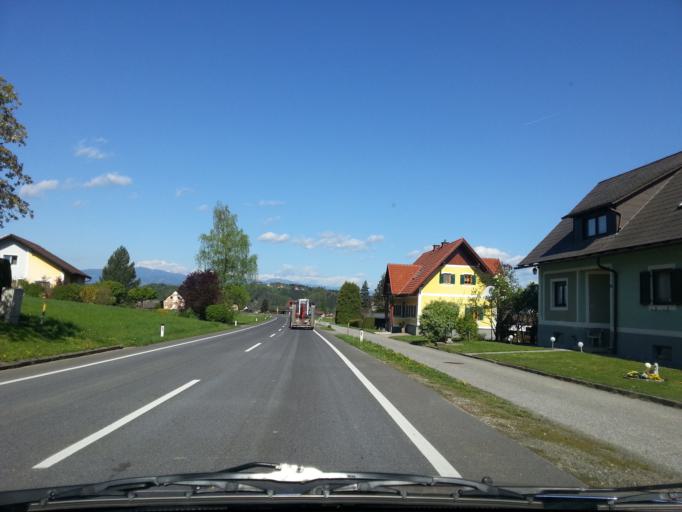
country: AT
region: Styria
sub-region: Politischer Bezirk Leibnitz
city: Arnfels
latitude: 46.6860
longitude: 15.3825
